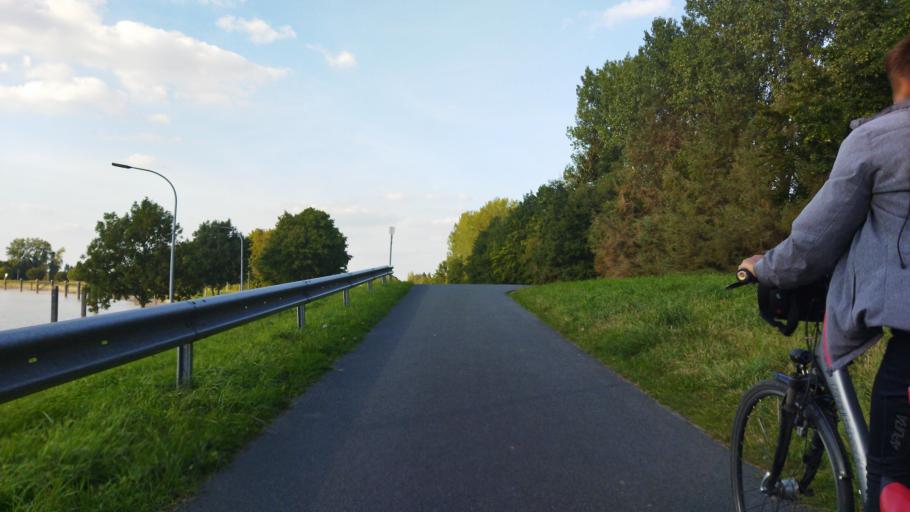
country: DE
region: Lower Saxony
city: Lehe
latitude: 53.0416
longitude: 7.3194
